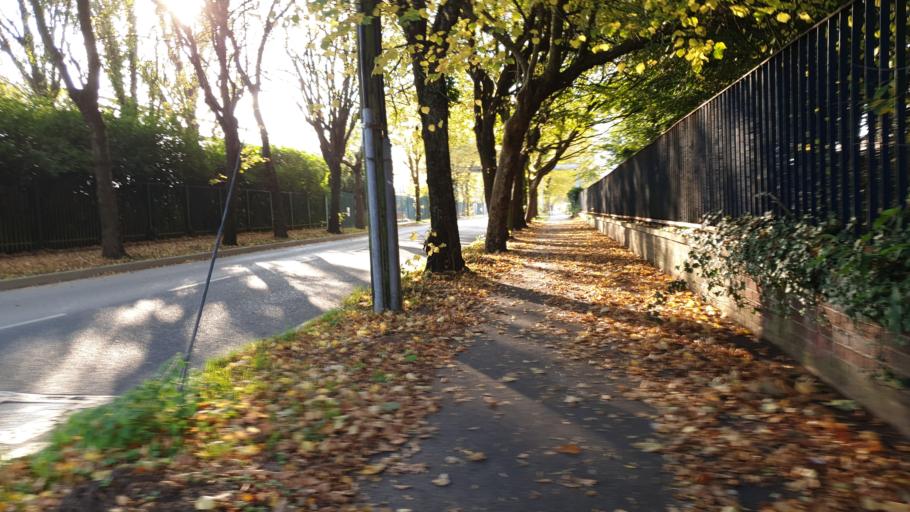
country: IE
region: Munster
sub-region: County Cork
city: Cork
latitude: 51.8984
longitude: -8.4451
